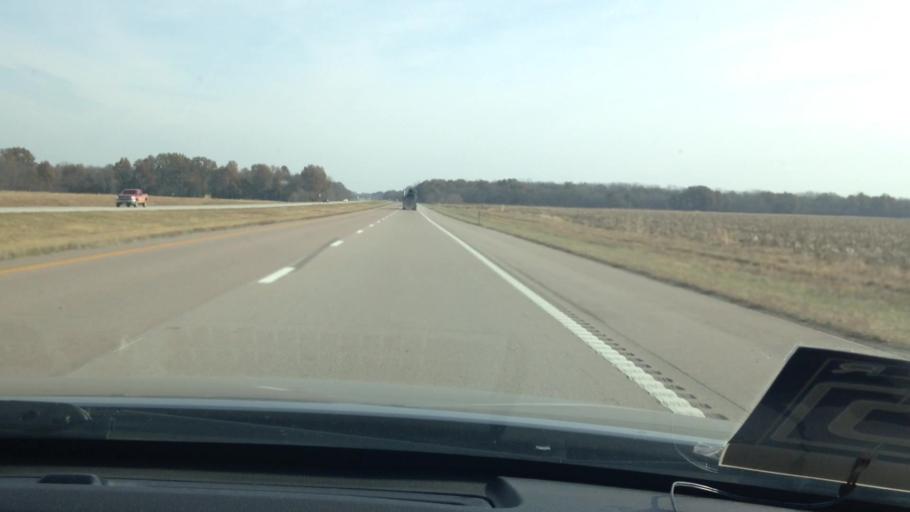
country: US
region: Missouri
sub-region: Henry County
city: Clinton
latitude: 38.4282
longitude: -93.9155
